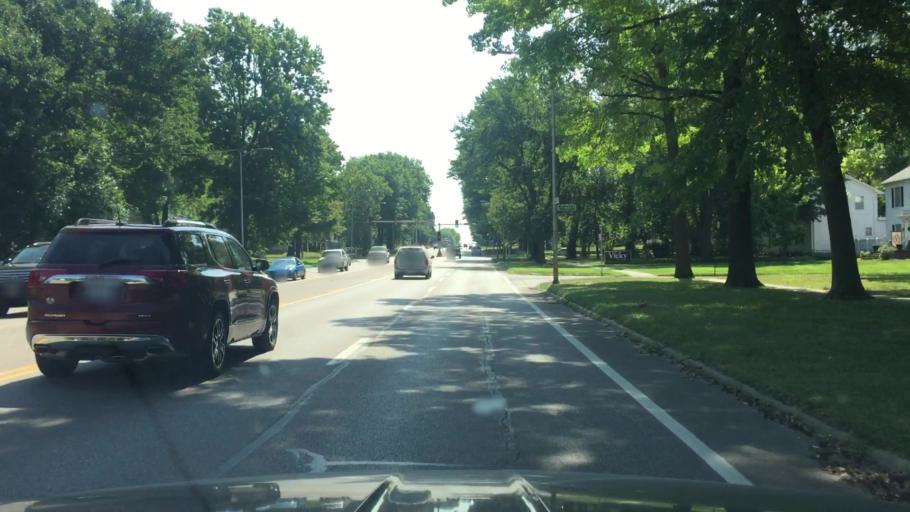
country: US
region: Missouri
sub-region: Pettis County
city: Sedalia
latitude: 38.7045
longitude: -93.2381
